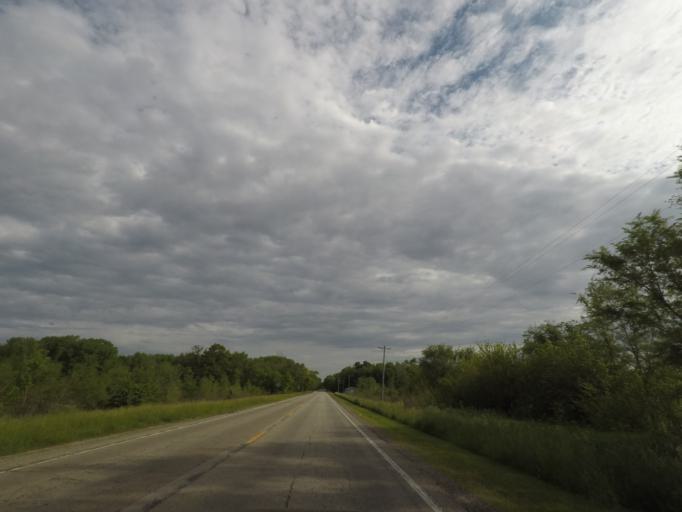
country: US
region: Illinois
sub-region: Logan County
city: Mount Pulaski
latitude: 40.0499
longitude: -89.2820
